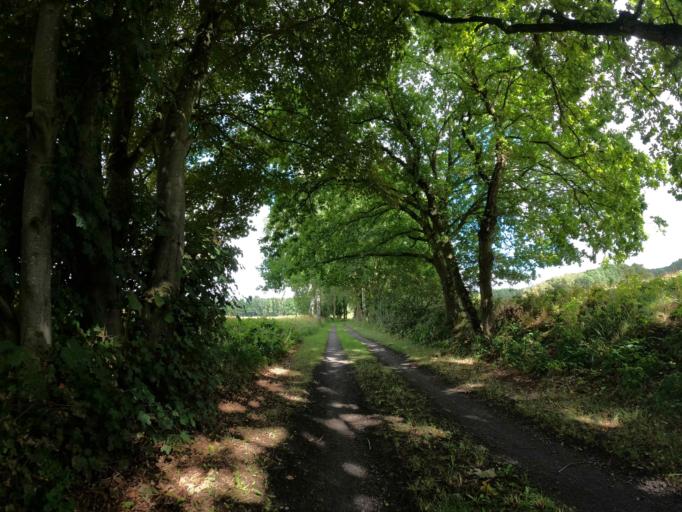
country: DE
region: Mecklenburg-Vorpommern
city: Sehlen
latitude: 54.3501
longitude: 13.3832
